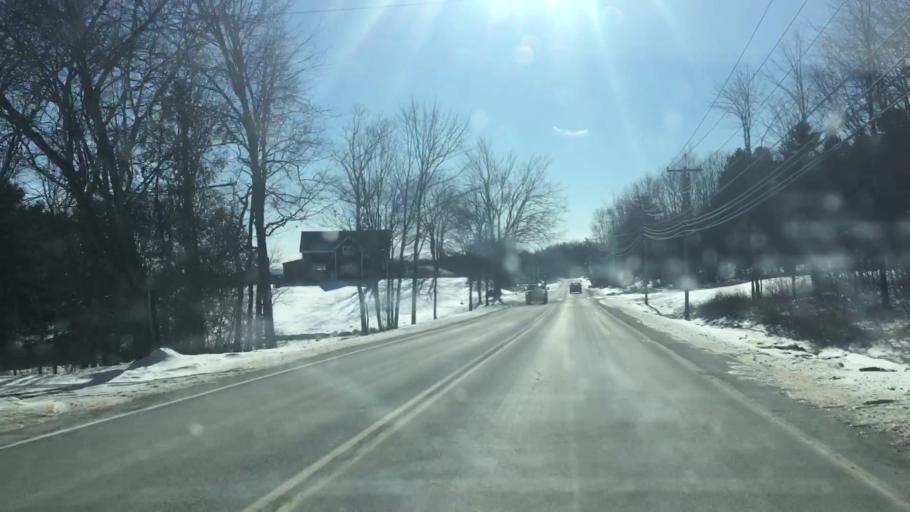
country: US
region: Maine
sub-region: Hancock County
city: Ellsworth
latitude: 44.5331
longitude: -68.4314
